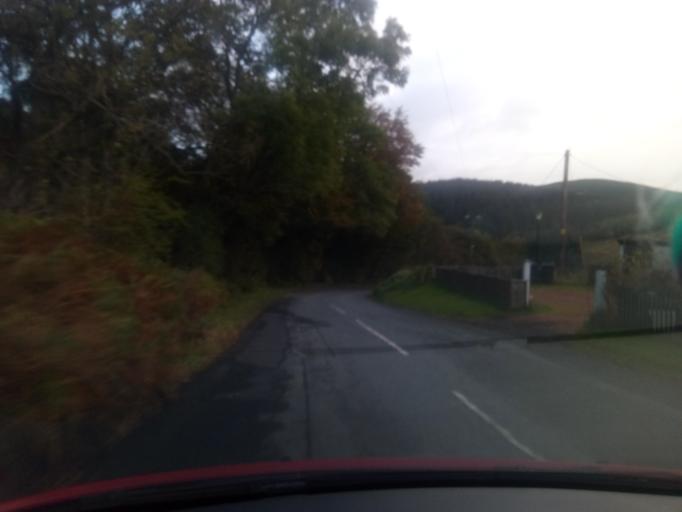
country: GB
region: Scotland
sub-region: The Scottish Borders
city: Hawick
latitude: 55.3455
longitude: -2.6497
